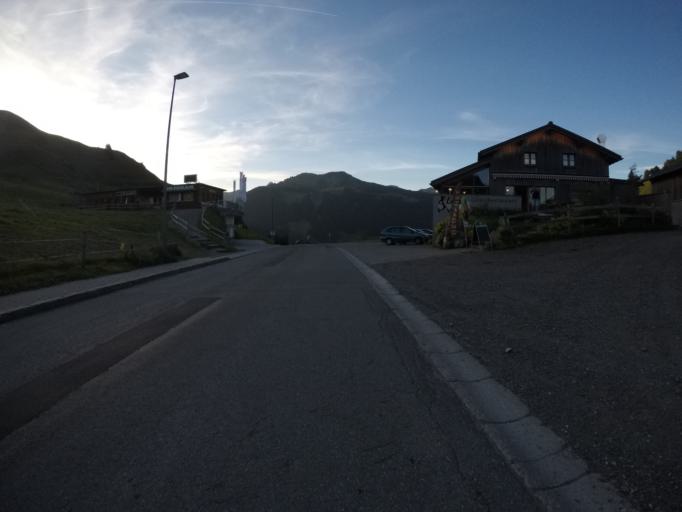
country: AT
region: Vorarlberg
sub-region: Politischer Bezirk Bregenz
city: Damuels
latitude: 47.2724
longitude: 9.9072
